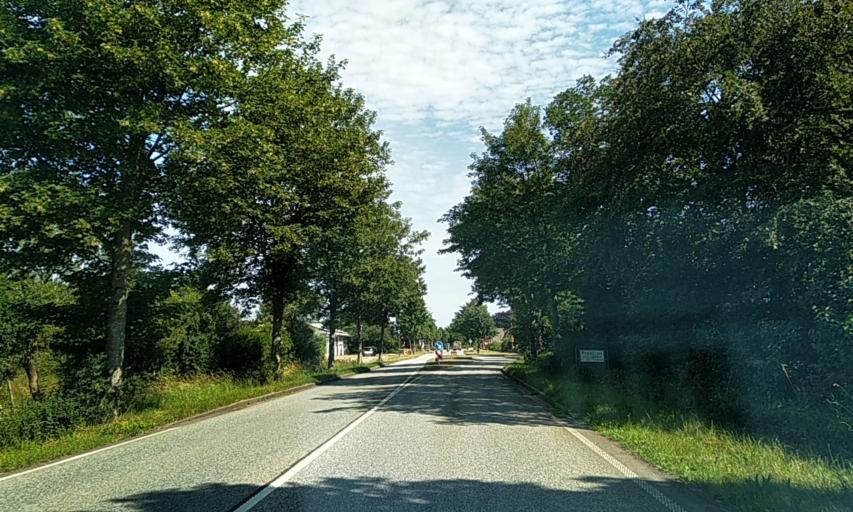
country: DE
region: Schleswig-Holstein
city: Jagel
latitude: 54.4517
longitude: 9.5371
